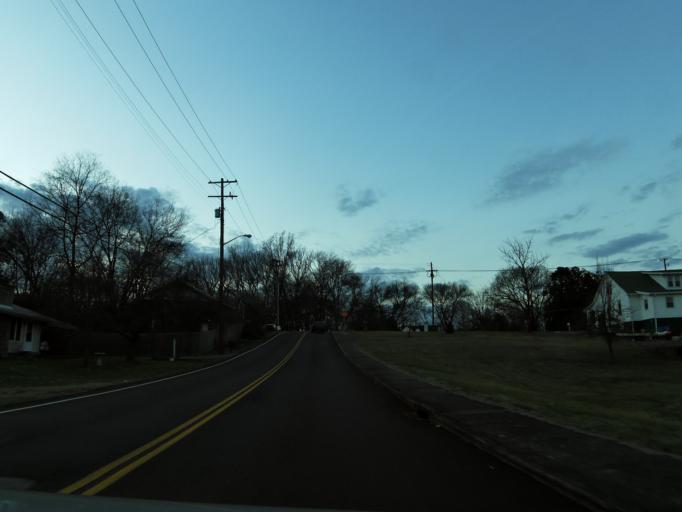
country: US
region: Tennessee
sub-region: Knox County
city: Knoxville
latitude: 35.9406
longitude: -83.8992
